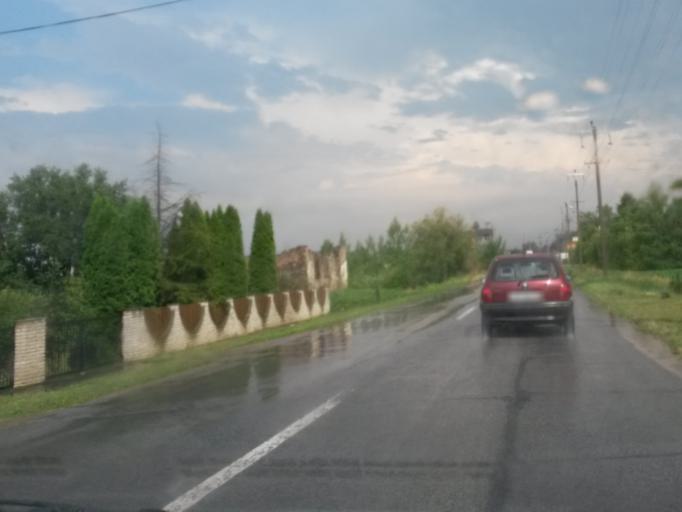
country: RS
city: Bogojevo
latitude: 45.5347
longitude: 19.1238
